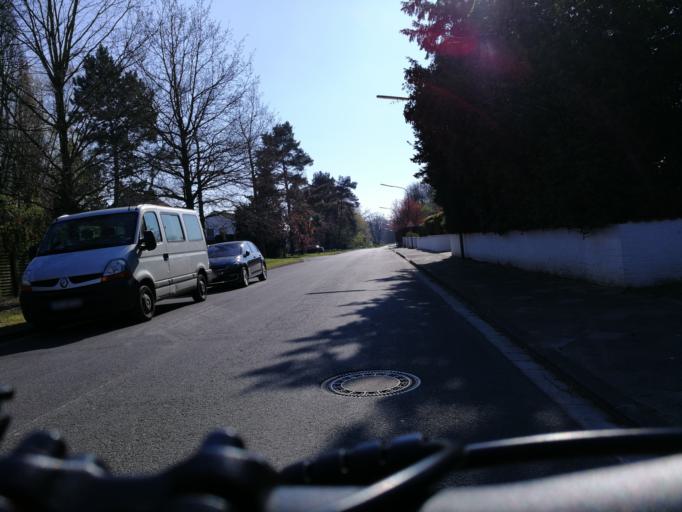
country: DE
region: North Rhine-Westphalia
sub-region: Regierungsbezirk Dusseldorf
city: Neuss
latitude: 51.1804
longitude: 6.7254
